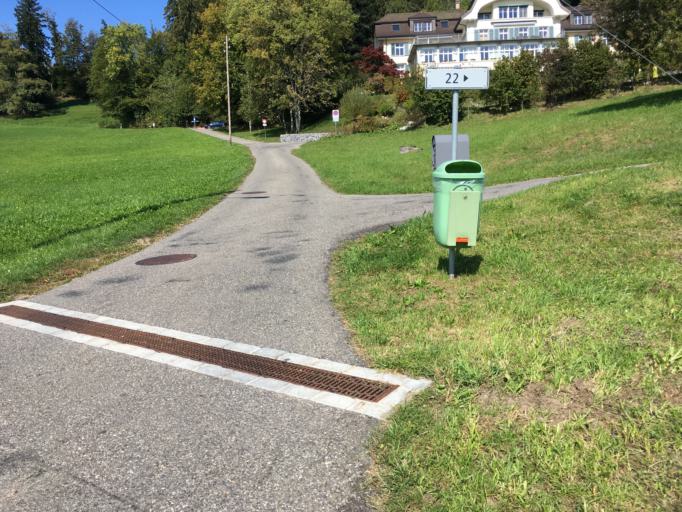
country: CH
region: Zurich
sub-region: Bezirk Hinwil
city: Baretswil
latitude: 47.3449
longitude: 8.8430
